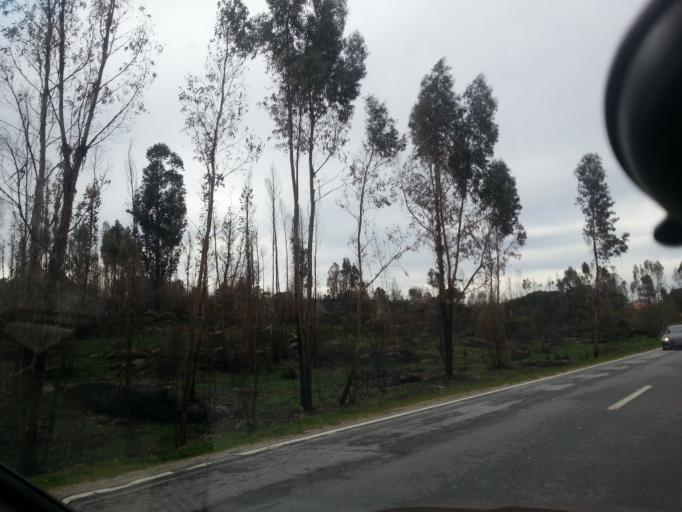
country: PT
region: Guarda
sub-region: Fornos de Algodres
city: Fornos de Algodres
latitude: 40.5197
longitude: -7.6204
